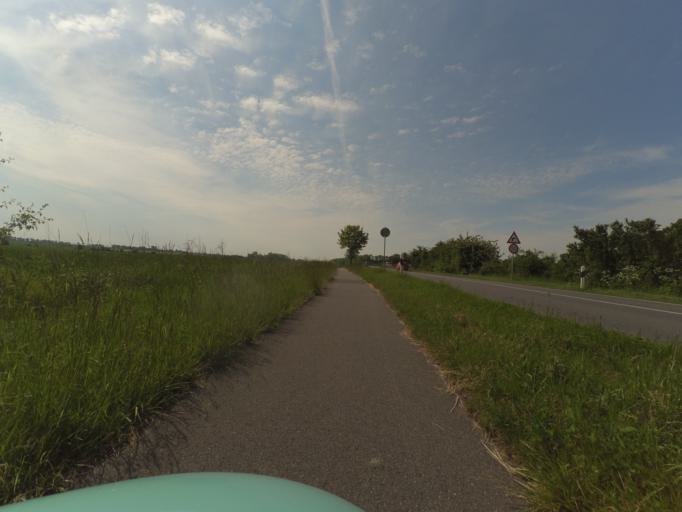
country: DE
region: Lower Saxony
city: Sehnde
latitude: 52.3038
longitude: 9.9619
